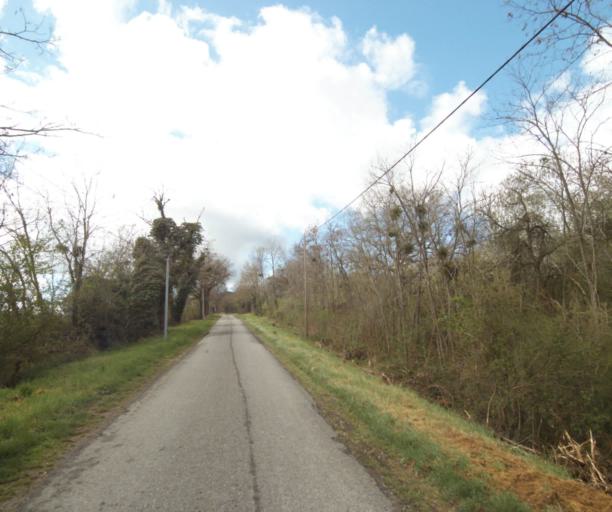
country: FR
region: Midi-Pyrenees
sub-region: Departement de l'Ariege
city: Saverdun
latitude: 43.2088
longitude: 1.5755
